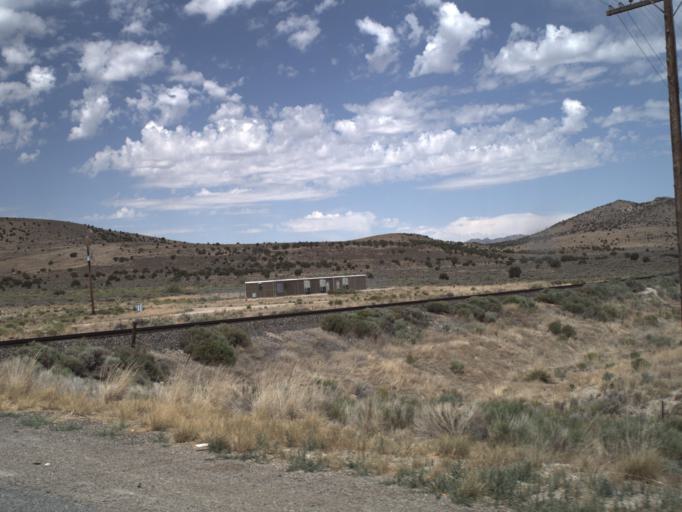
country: US
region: Utah
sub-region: Utah County
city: Eagle Mountain
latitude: 40.0761
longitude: -112.3499
